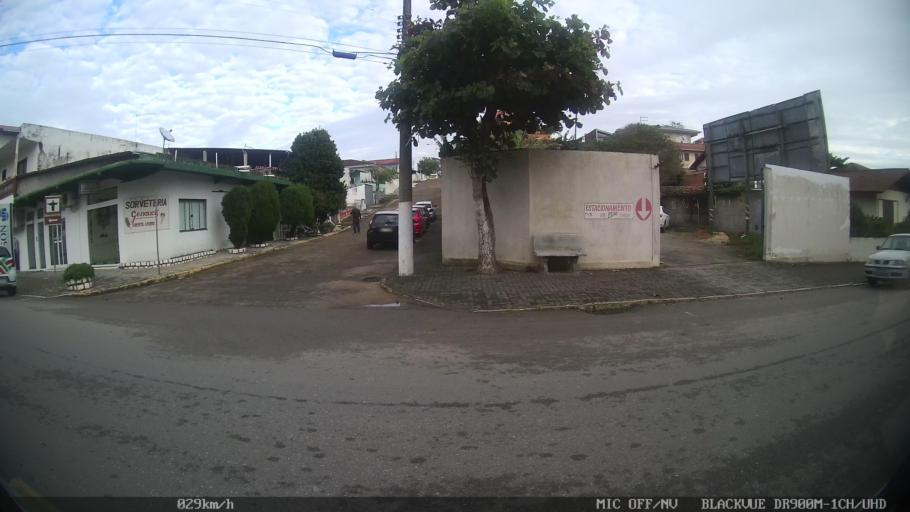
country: BR
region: Santa Catarina
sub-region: Barra Velha
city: Barra Velha
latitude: -26.6348
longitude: -48.6850
